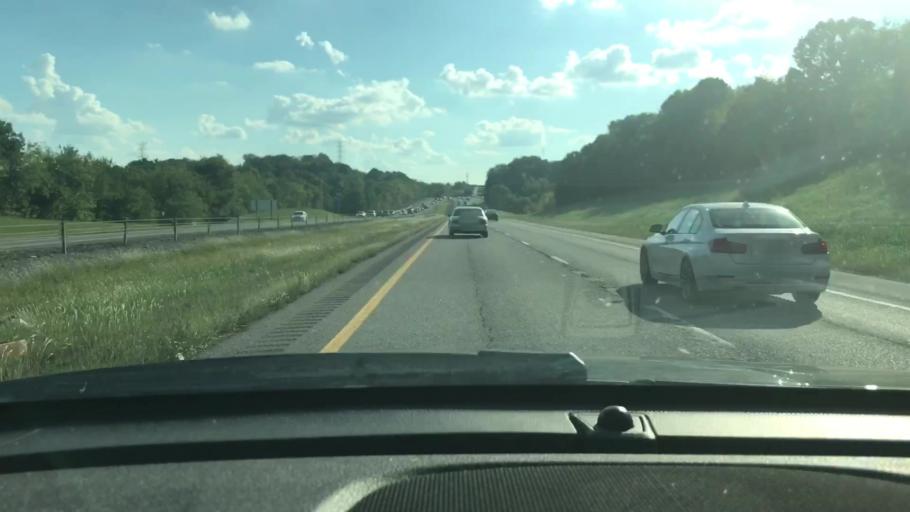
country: US
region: Tennessee
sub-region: Sumner County
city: Hendersonville
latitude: 36.3258
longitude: -86.6333
